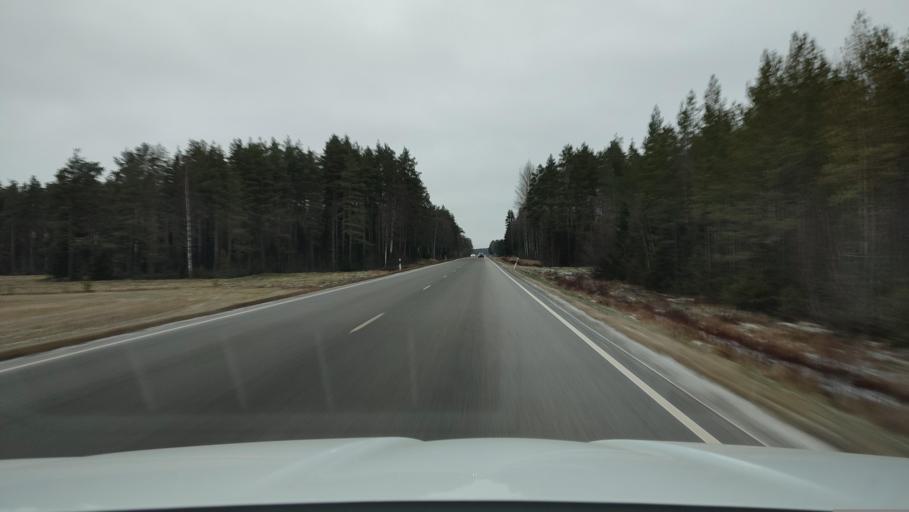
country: FI
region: Ostrobothnia
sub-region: Sydosterbotten
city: Naerpes
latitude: 62.5299
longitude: 21.4620
